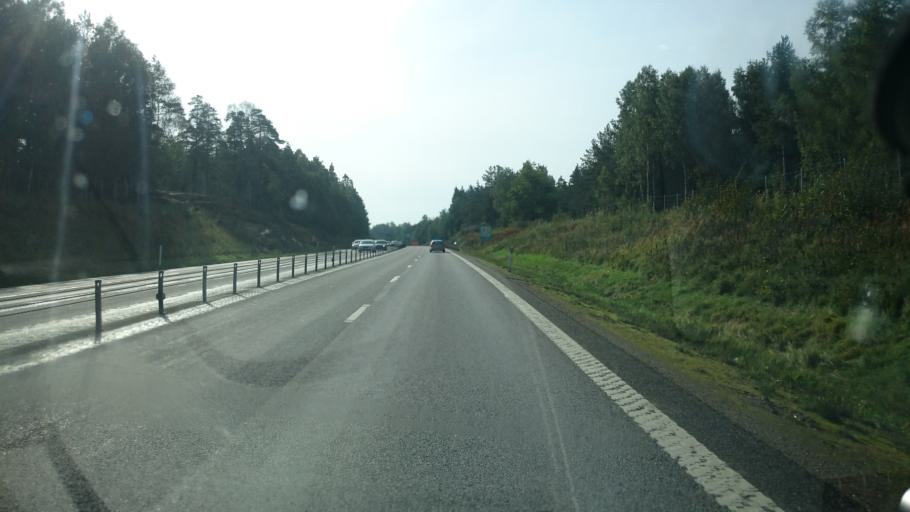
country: SE
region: Vaestra Goetaland
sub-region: Trollhattan
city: Trollhattan
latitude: 58.3292
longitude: 12.2979
